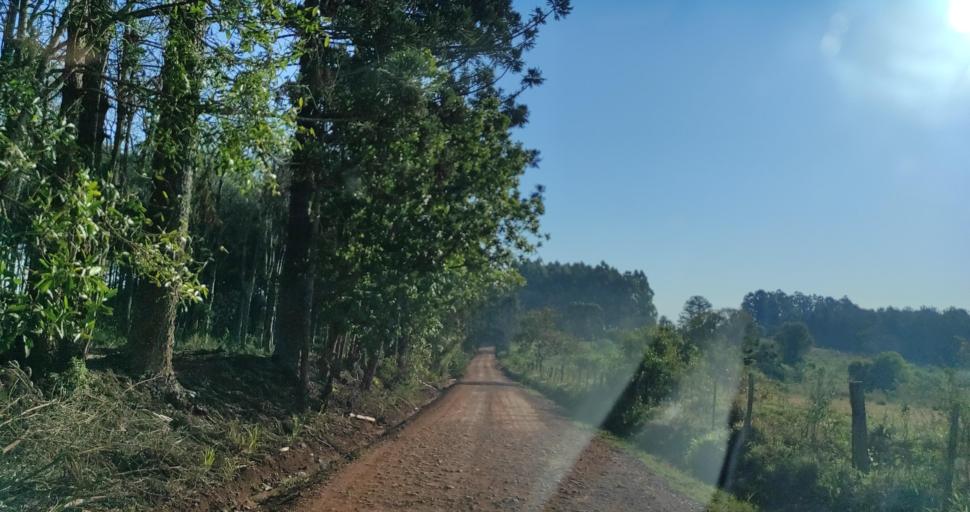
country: AR
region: Misiones
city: Capiovi
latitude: -26.8735
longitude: -55.1100
